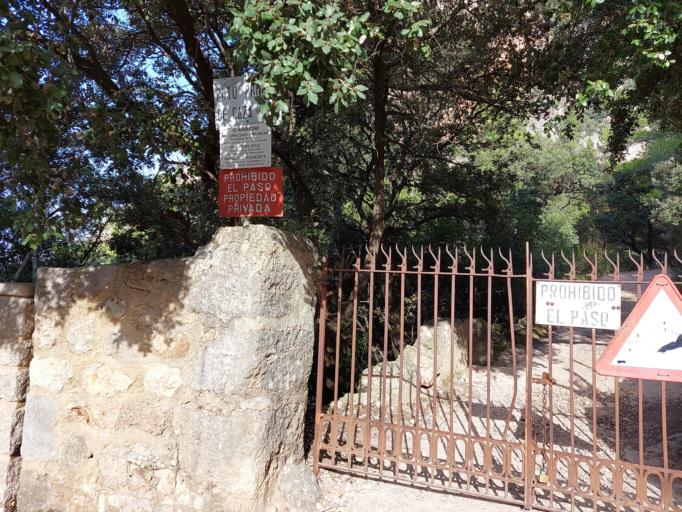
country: ES
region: Balearic Islands
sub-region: Illes Balears
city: Soller
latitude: 39.7543
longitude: 2.7247
